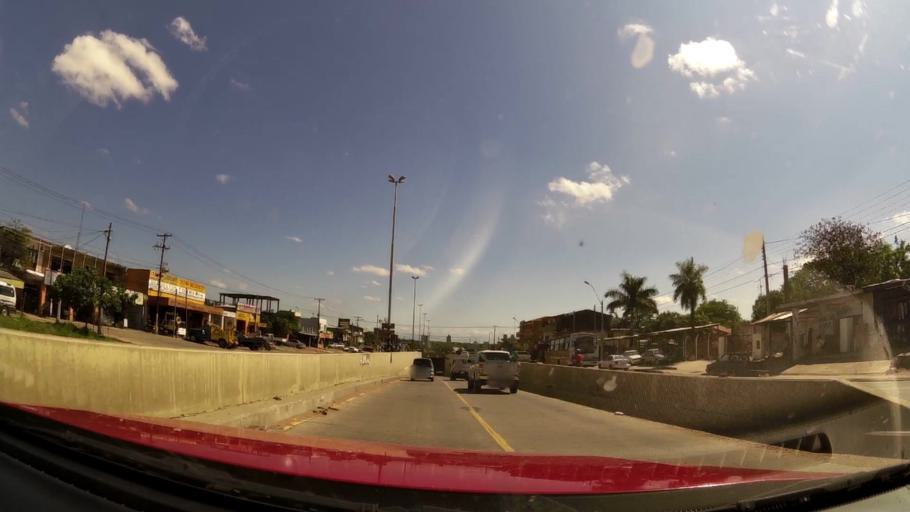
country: PY
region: Central
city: Colonia Mariano Roque Alonso
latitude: -25.2455
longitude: -57.5483
